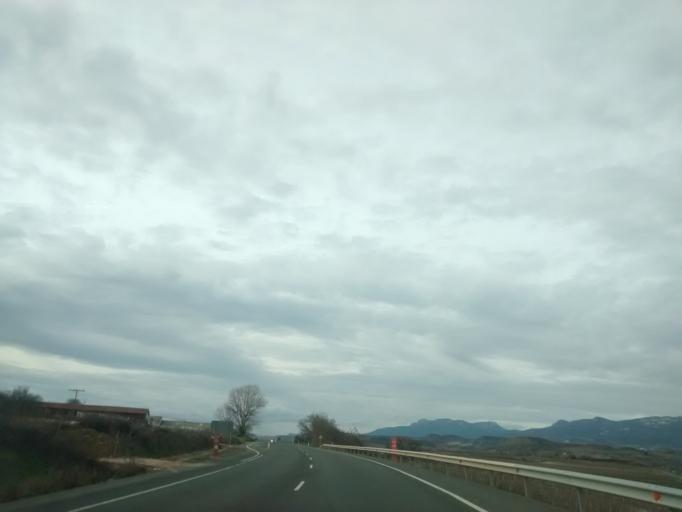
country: ES
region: La Rioja
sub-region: Provincia de La Rioja
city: Cenicero
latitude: 42.4871
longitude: -2.6585
